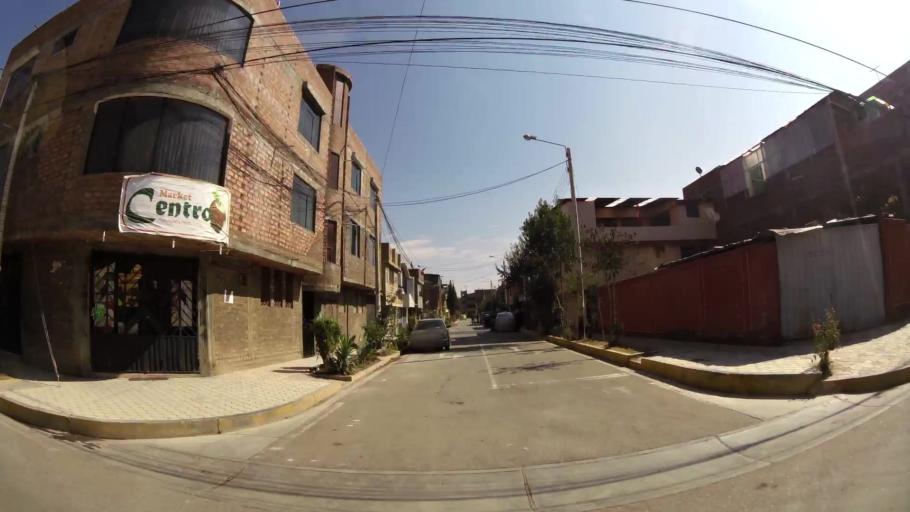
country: PE
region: Junin
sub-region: Provincia de Huancayo
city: El Tambo
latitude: -12.0756
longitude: -75.2277
